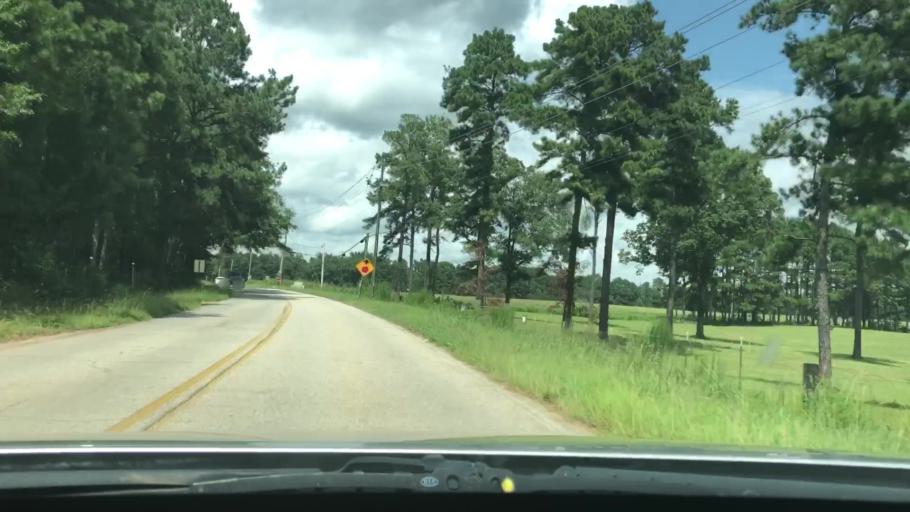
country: US
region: Georgia
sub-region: Henry County
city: McDonough
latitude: 33.4017
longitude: -84.1196
